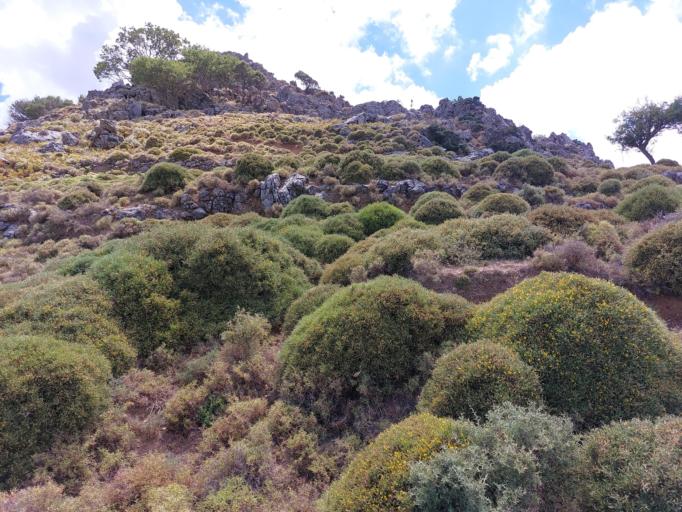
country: GR
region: Crete
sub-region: Nomos Chanias
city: Vryses
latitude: 35.4142
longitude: 23.6575
